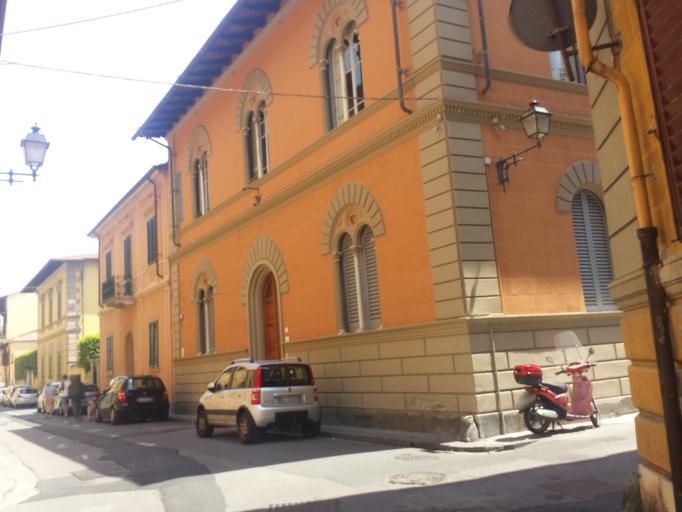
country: IT
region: Tuscany
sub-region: Province of Pisa
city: Pisa
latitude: 43.7214
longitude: 10.4002
